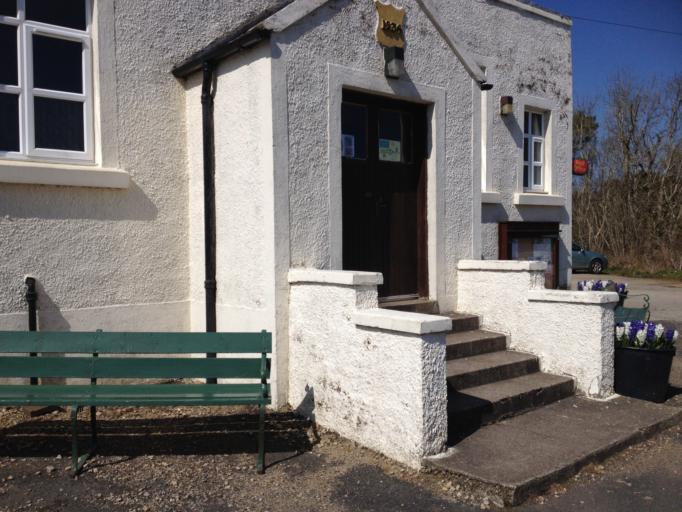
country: GB
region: Scotland
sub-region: North Ayrshire
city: Lamlash
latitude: 55.4445
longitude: -5.2317
